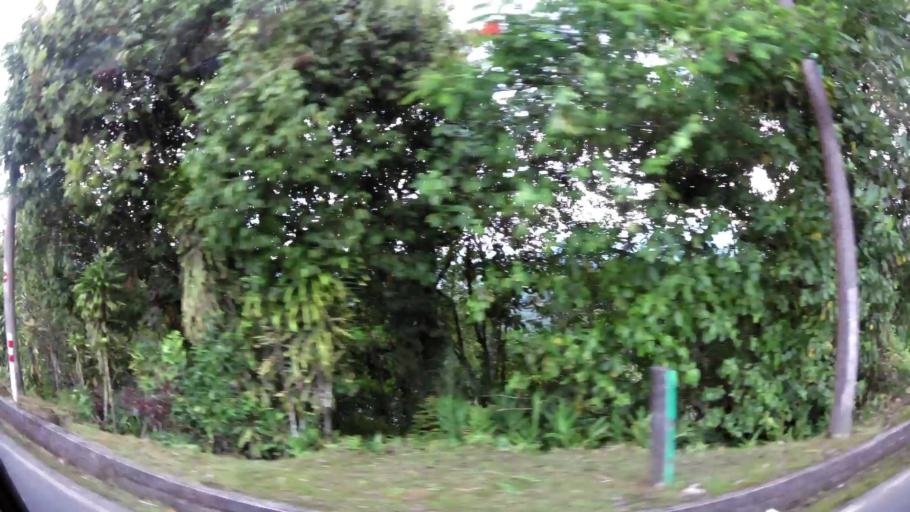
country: EC
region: Pastaza
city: Puyo
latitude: -1.4588
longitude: -78.1174
